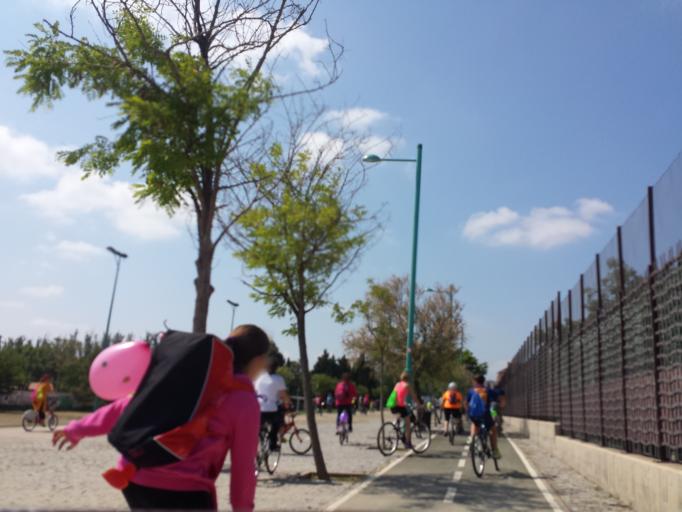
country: ES
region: Aragon
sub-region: Provincia de Zaragoza
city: Almozara
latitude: 41.6656
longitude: -0.8999
